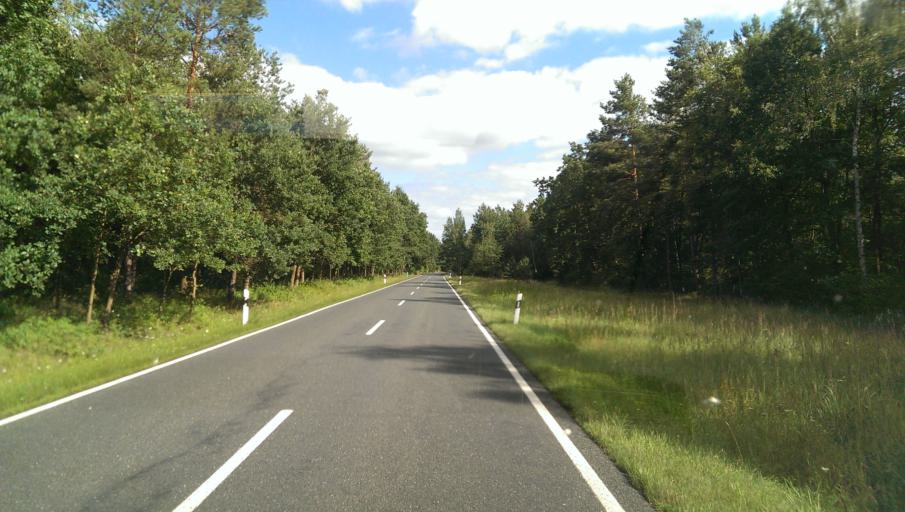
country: DE
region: Saxony-Anhalt
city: Radis
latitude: 51.7611
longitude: 12.5022
